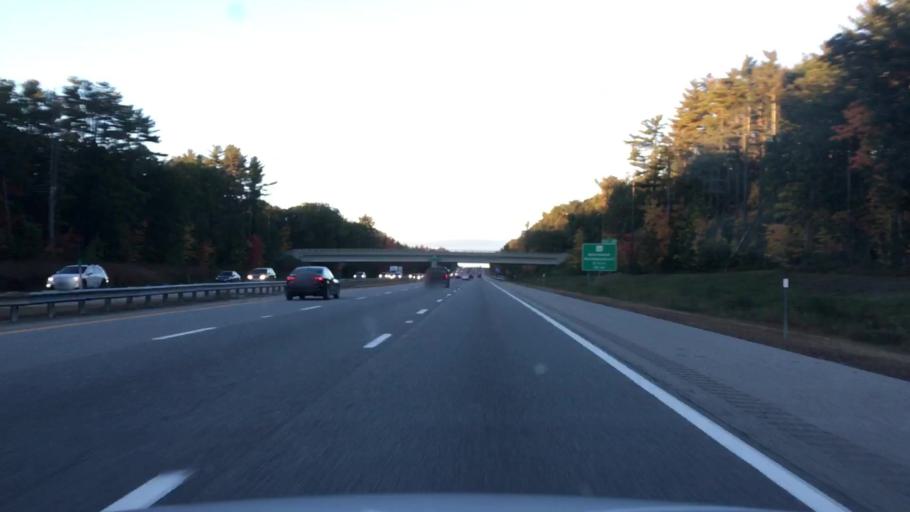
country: US
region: Maine
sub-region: York County
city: West Kennebunk
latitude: 43.3793
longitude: -70.5768
